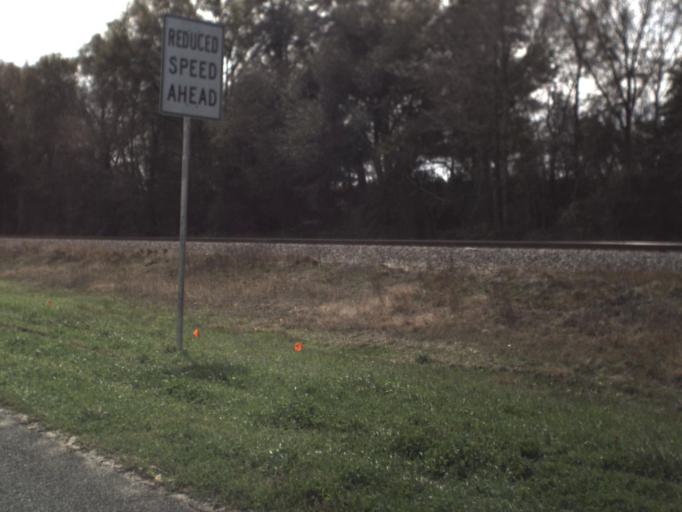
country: US
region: Florida
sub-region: Washington County
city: Chipley
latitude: 30.6654
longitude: -85.3931
